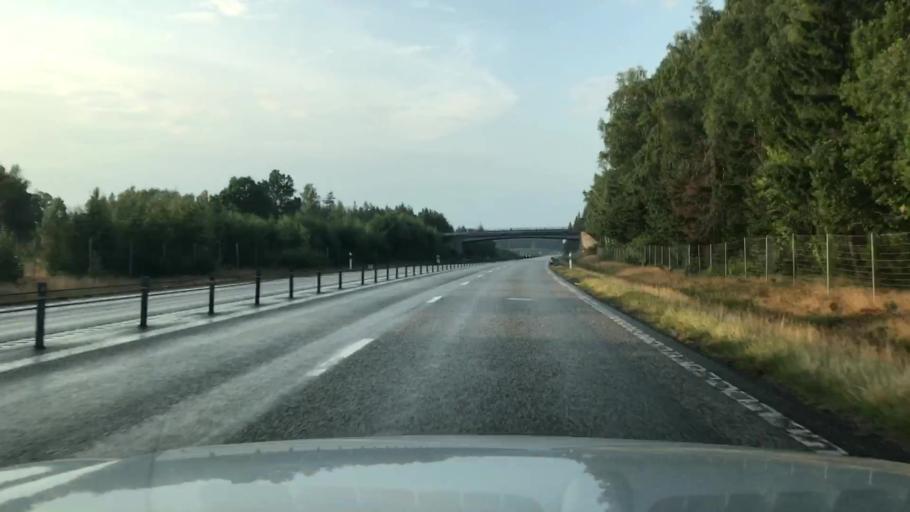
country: SE
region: Kronoberg
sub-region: Ljungby Kommun
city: Lagan
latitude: 56.9854
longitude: 14.0196
